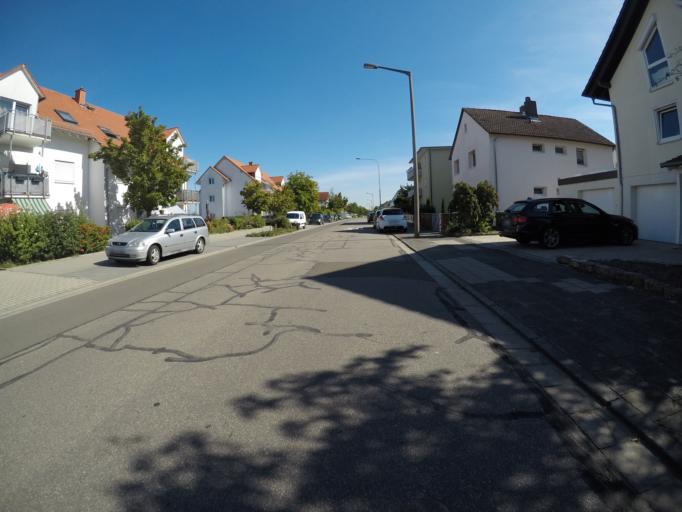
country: DE
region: Hesse
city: Lampertheim
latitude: 49.6054
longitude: 8.4704
